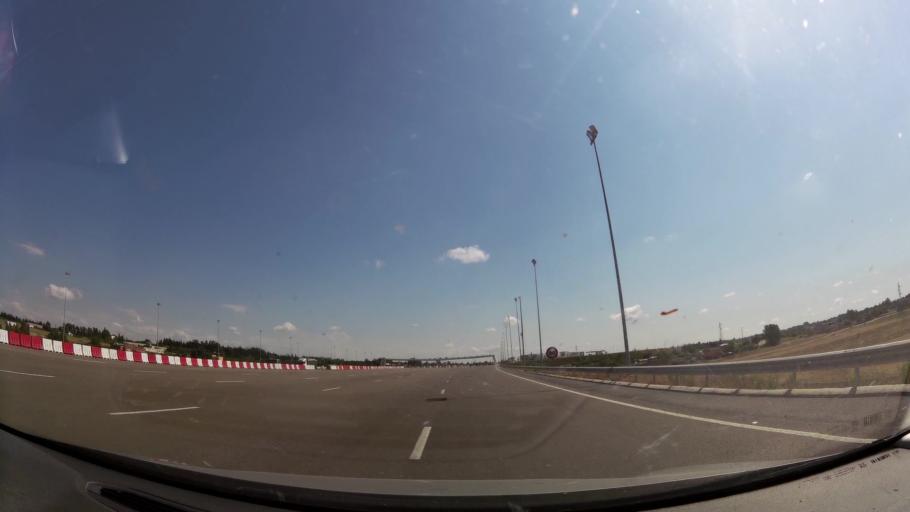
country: MA
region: Rabat-Sale-Zemmour-Zaer
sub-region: Rabat
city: Rabat
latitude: 33.9677
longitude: -6.7407
